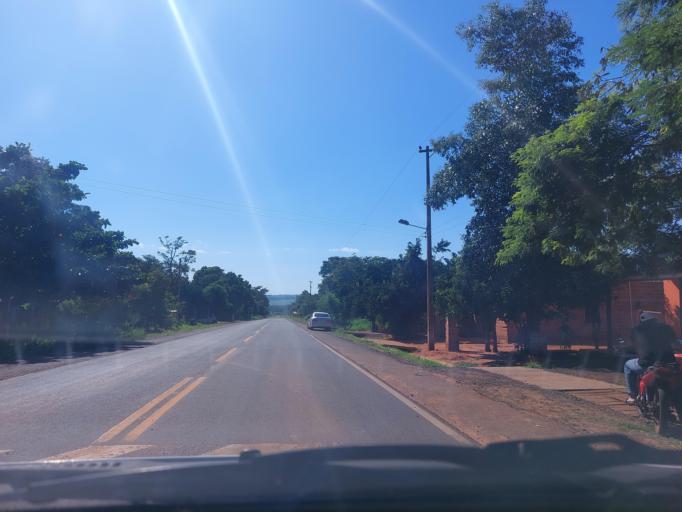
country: PY
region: San Pedro
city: Guayaybi
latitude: -24.3144
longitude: -56.1590
